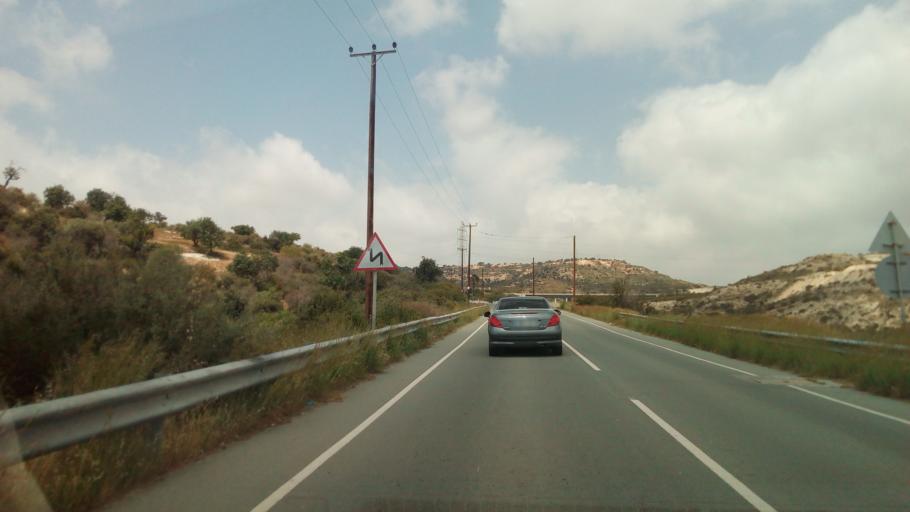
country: CY
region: Limassol
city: Pissouri
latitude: 34.6795
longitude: 32.7153
